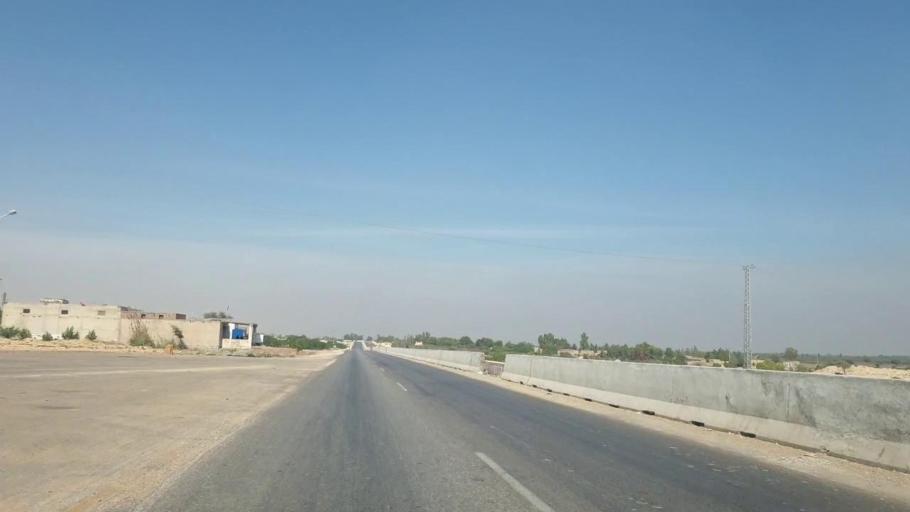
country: PK
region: Sindh
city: Hala
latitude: 25.7055
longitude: 68.2958
